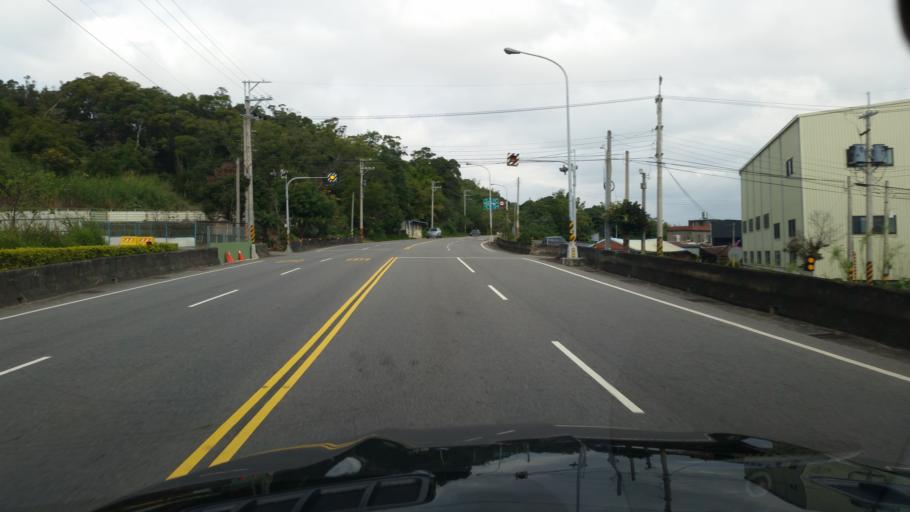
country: TW
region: Taiwan
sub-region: Miaoli
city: Miaoli
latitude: 24.6525
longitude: 120.8645
